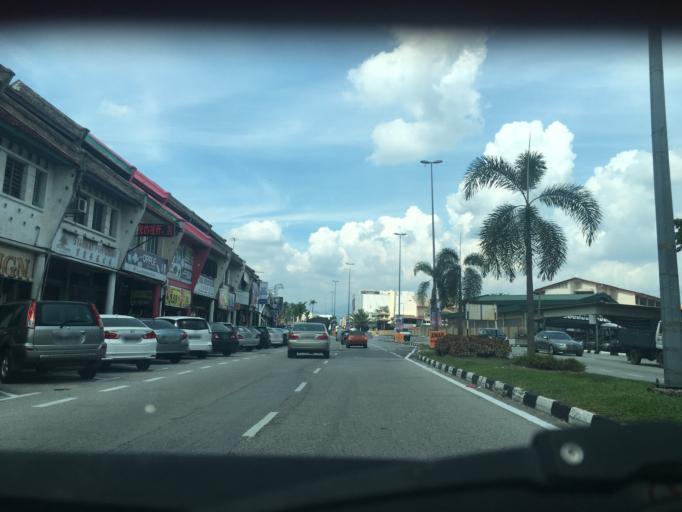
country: MY
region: Perak
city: Ipoh
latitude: 4.5858
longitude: 101.0827
